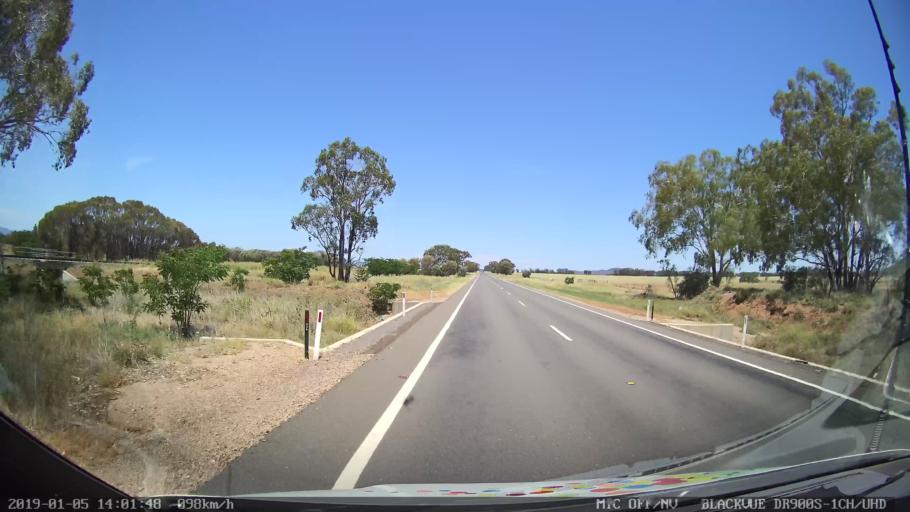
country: AU
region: New South Wales
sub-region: Gunnedah
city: Gunnedah
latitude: -31.1734
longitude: 150.3297
